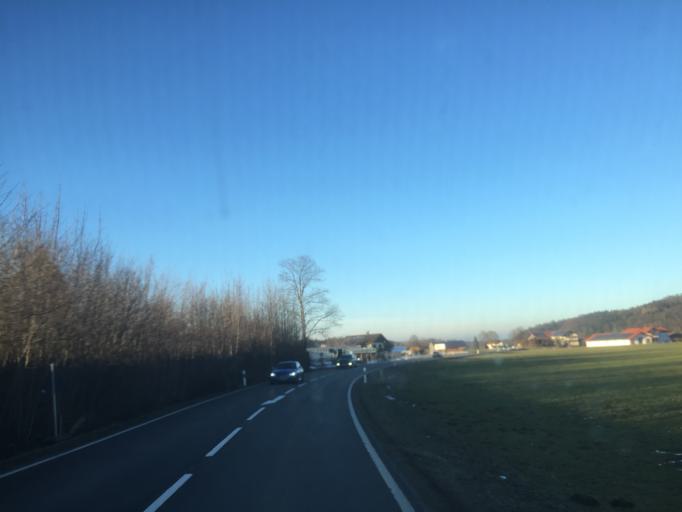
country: DE
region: Bavaria
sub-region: Upper Bavaria
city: Siegsdorf
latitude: 47.8341
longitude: 12.6349
